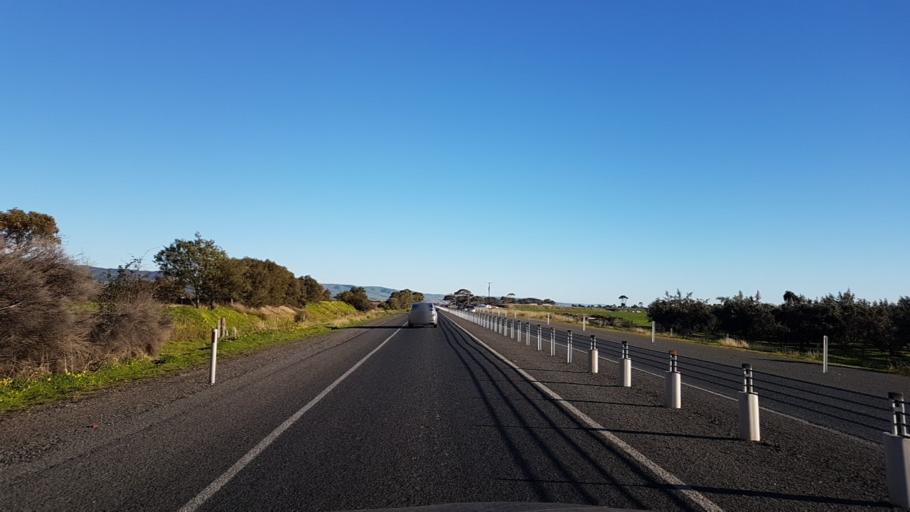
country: AU
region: South Australia
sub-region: Onkaparinga
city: Aldinga
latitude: -35.2557
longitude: 138.4935
